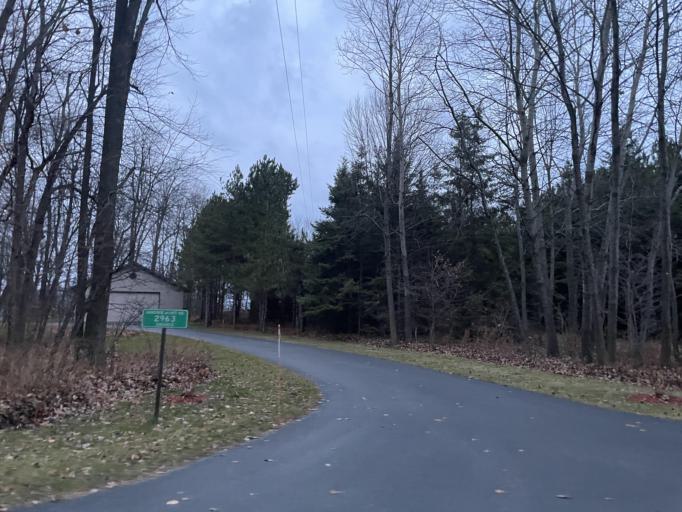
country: US
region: Wisconsin
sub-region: Oconto County
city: Oconto
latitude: 44.8145
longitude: -87.6338
